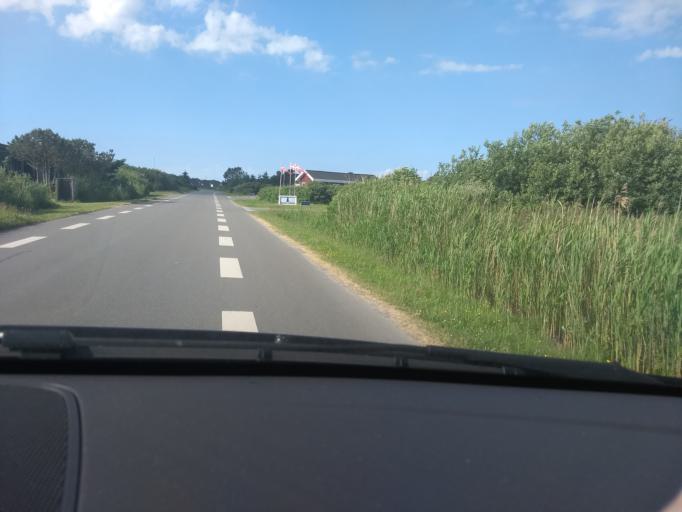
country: DE
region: Schleswig-Holstein
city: List
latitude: 55.1393
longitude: 8.4945
